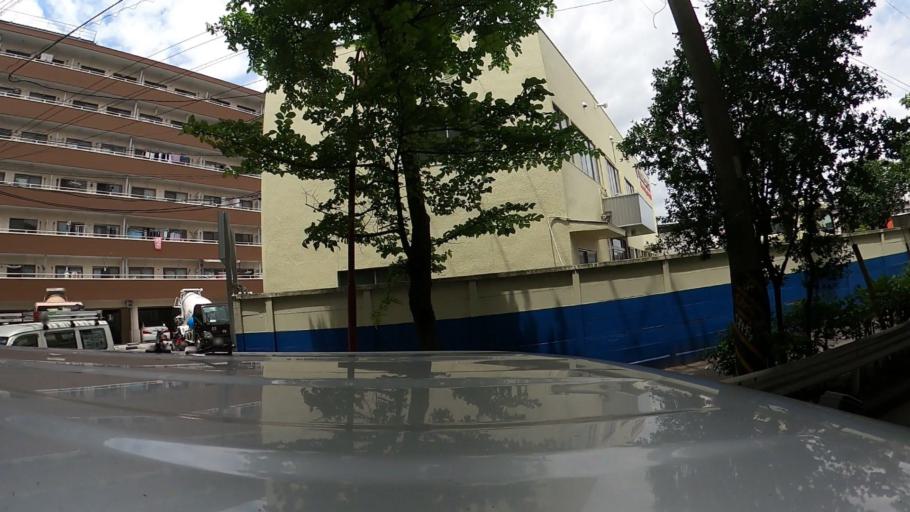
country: JP
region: Kanagawa
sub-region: Kawasaki-shi
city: Kawasaki
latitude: 35.5032
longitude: 139.6999
